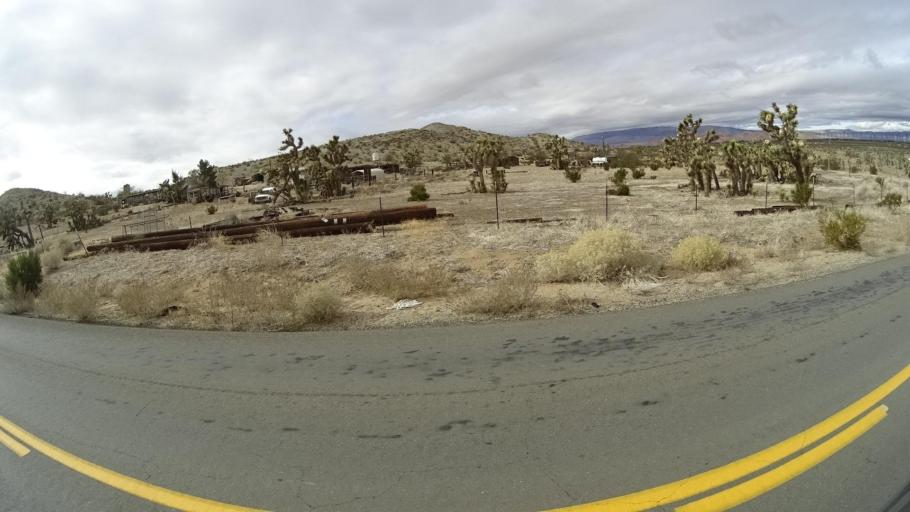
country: US
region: California
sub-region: Kern County
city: Rosamond
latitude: 34.9246
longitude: -118.2123
